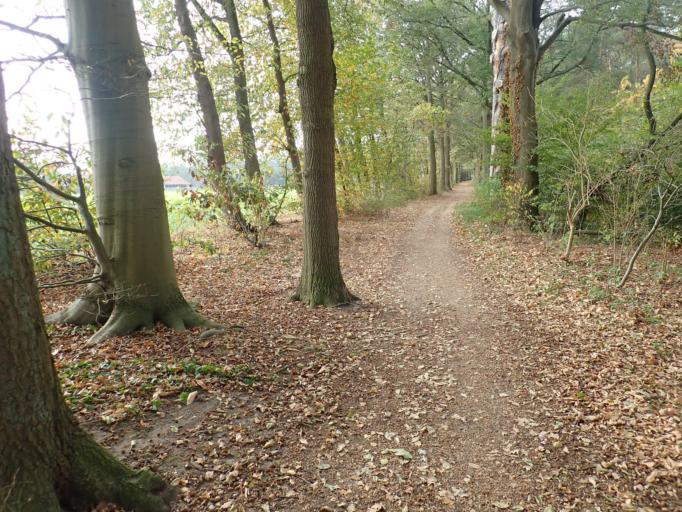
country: BE
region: Flanders
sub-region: Provincie Antwerpen
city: Herenthout
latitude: 51.1376
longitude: 4.7381
